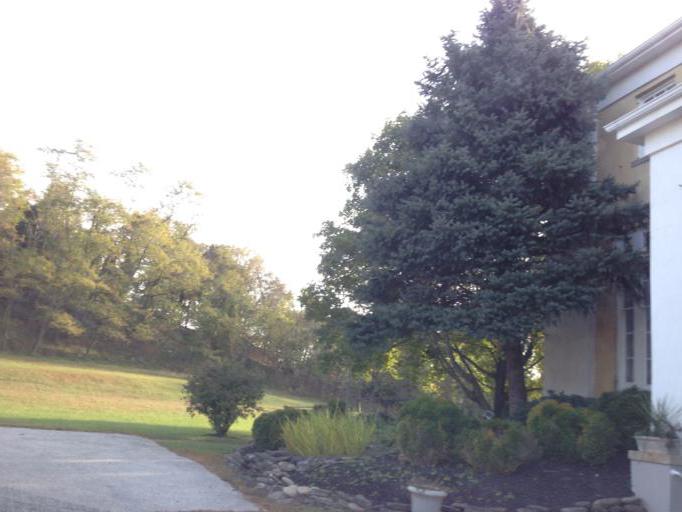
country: US
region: Maryland
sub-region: Howard County
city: Ellicott City
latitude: 39.2691
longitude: -76.7967
